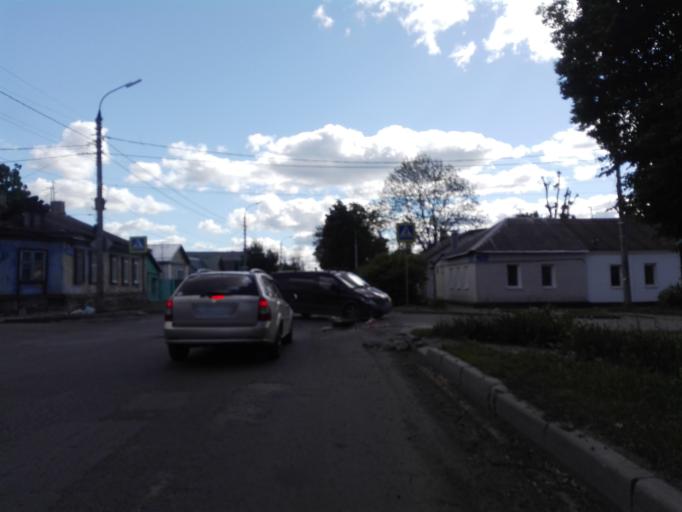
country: RU
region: Orjol
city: Orel
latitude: 52.9587
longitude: 36.0574
